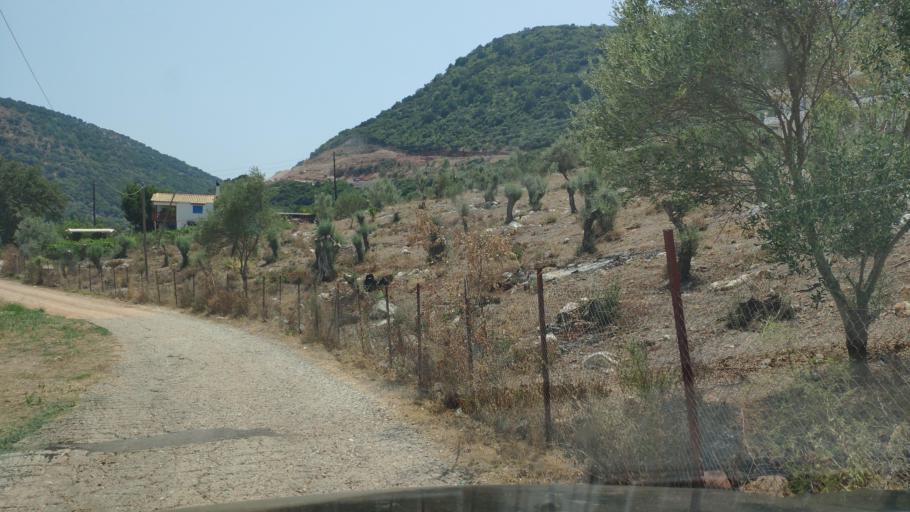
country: GR
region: West Greece
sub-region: Nomos Aitolias kai Akarnanias
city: Amfilochia
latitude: 38.8674
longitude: 21.0749
